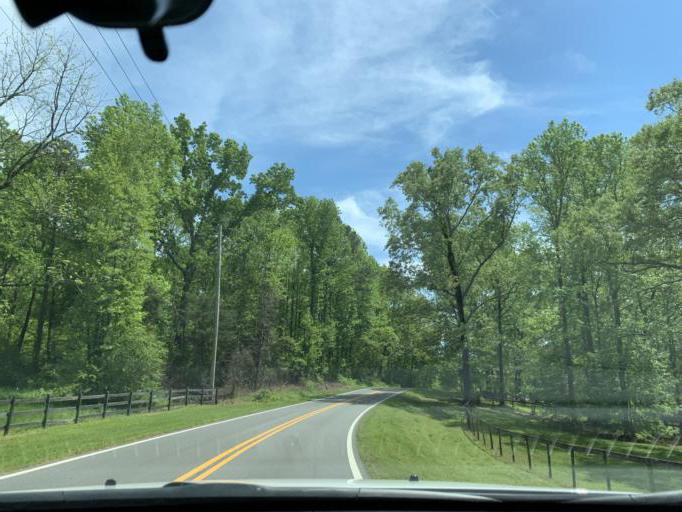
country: US
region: Georgia
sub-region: Hall County
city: Flowery Branch
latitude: 34.2681
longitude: -84.0232
